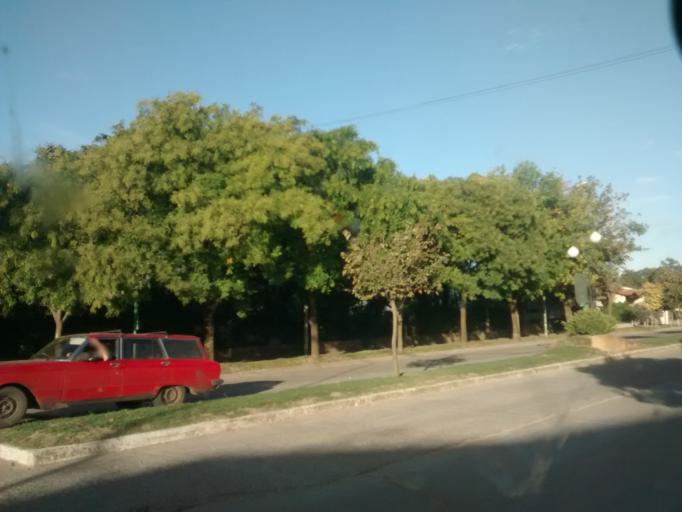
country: AR
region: Buenos Aires
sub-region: Partido de Loberia
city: Loberia
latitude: -38.1708
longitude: -58.7736
